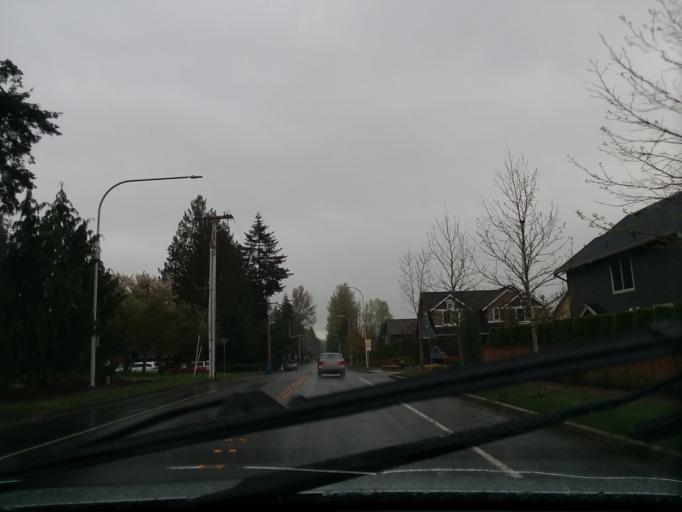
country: US
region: Washington
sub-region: King County
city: East Renton Highlands
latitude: 47.4861
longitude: -122.1483
